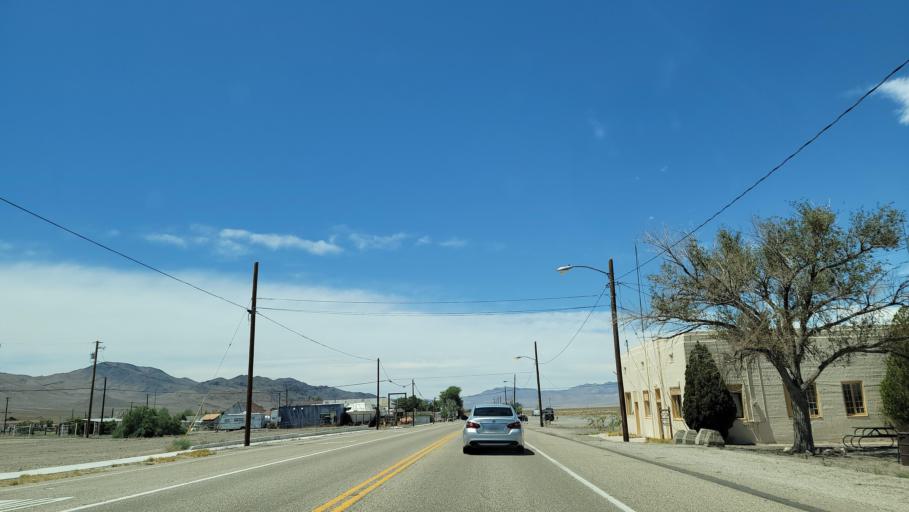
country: US
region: Nevada
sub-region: Mineral County
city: Hawthorne
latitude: 38.3908
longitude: -118.1088
